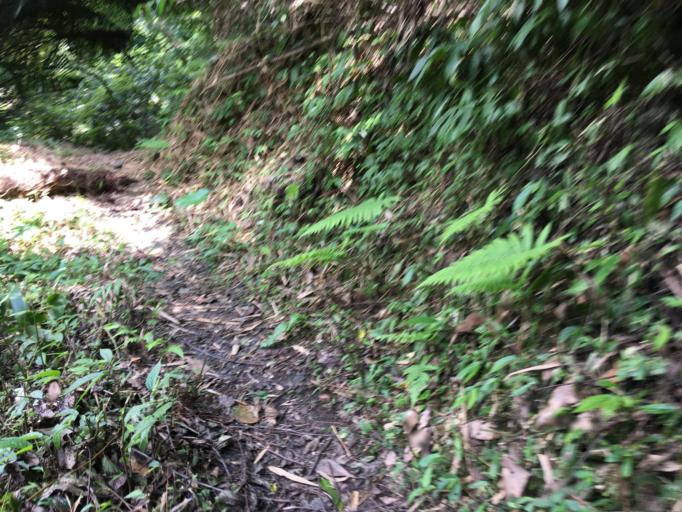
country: TW
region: Taiwan
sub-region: Yilan
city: Yilan
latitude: 24.4225
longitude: 121.6956
